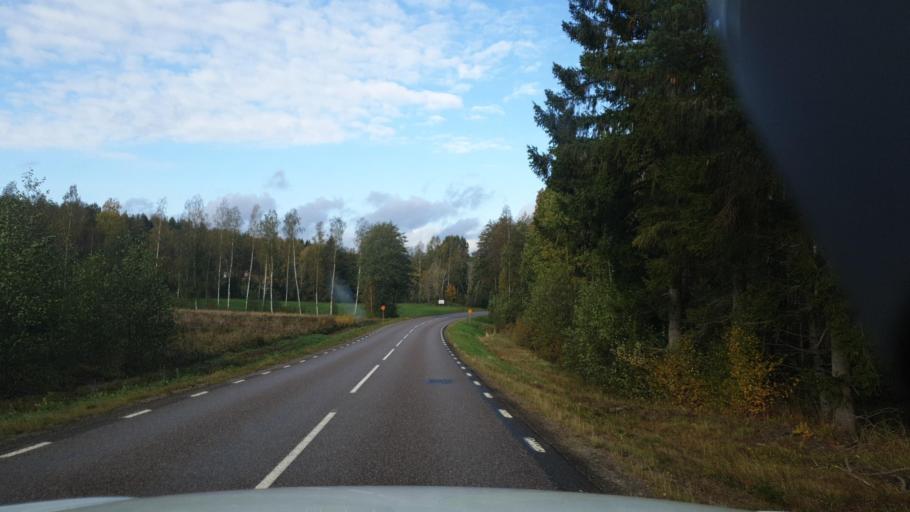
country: SE
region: Vaermland
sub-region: Arvika Kommun
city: Arvika
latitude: 59.4771
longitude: 12.7156
